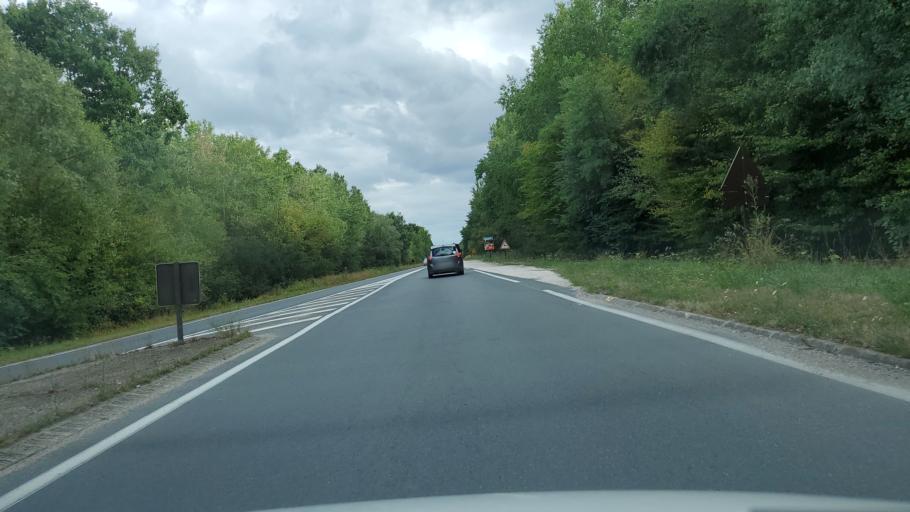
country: FR
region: Ile-de-France
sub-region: Departement de Seine-et-Marne
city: Villeneuve-le-Comte
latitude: 48.8145
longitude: 2.8419
